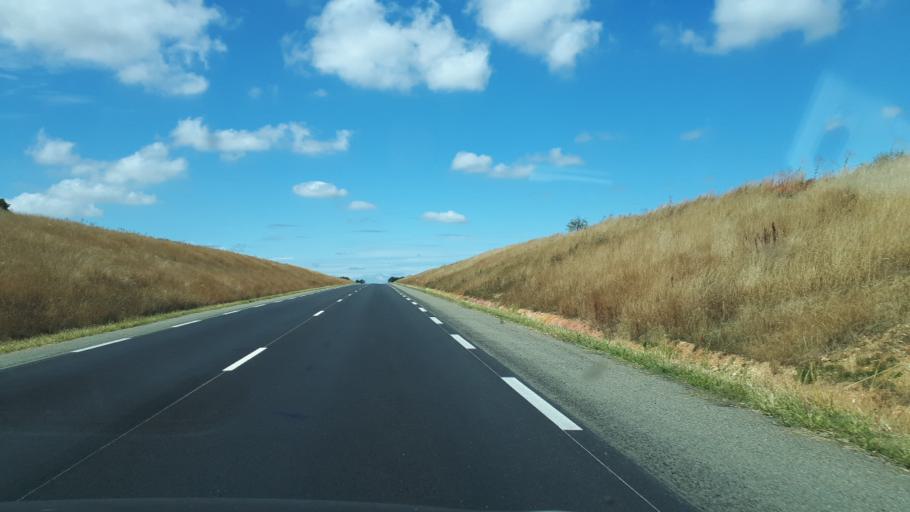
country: FR
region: Pays de la Loire
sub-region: Departement de la Sarthe
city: Saint-Calais
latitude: 47.9340
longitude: 0.7344
